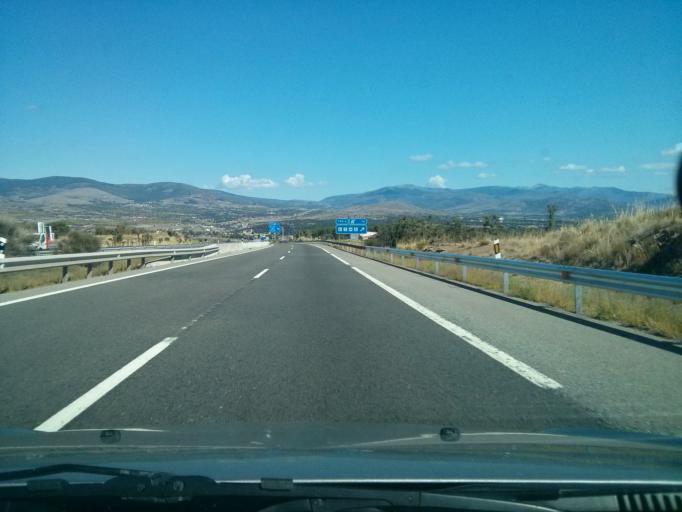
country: ES
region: Madrid
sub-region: Provincia de Madrid
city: Buitrago del Lozoya
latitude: 40.9688
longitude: -3.6406
